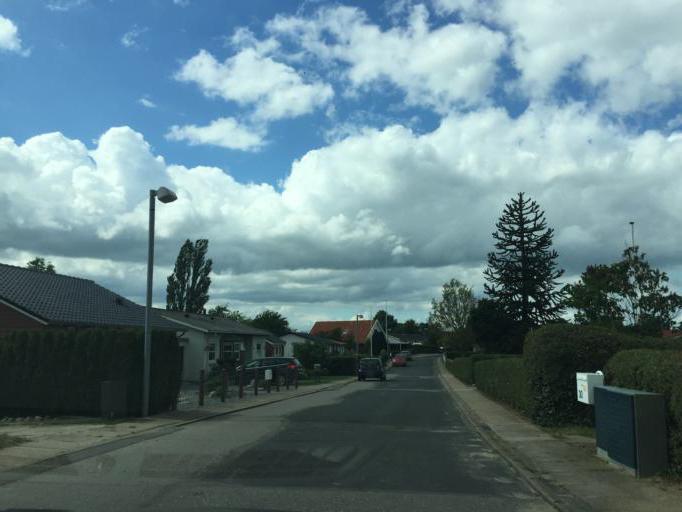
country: DK
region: South Denmark
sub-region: Odense Kommune
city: Odense
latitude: 55.4186
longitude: 10.3499
